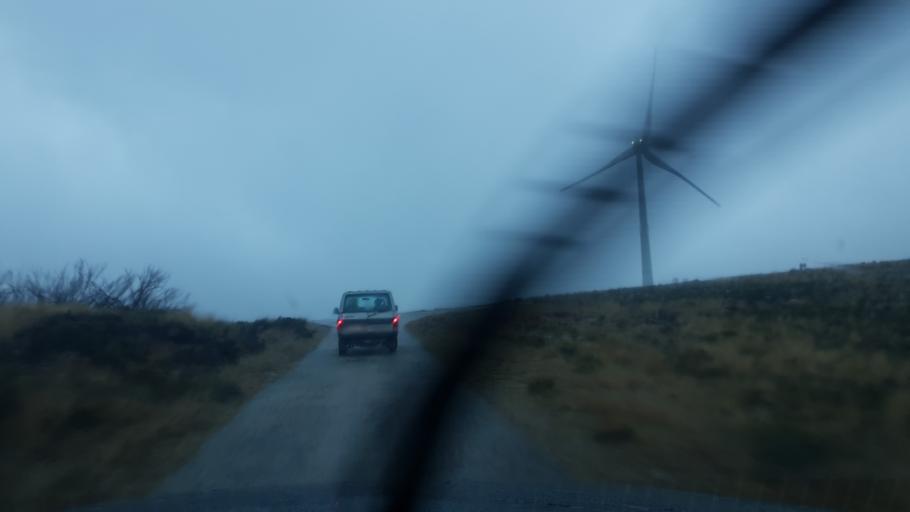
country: PT
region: Viseu
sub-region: Sao Pedro do Sul
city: Sao Pedro do Sul
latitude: 40.8307
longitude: -8.1239
